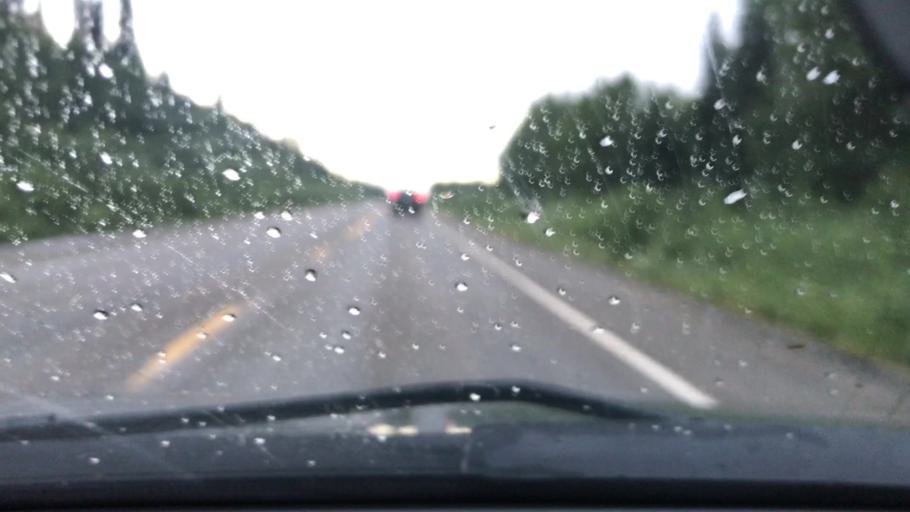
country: US
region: Alaska
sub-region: Matanuska-Susitna Borough
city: Y
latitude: 63.0400
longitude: -149.5849
